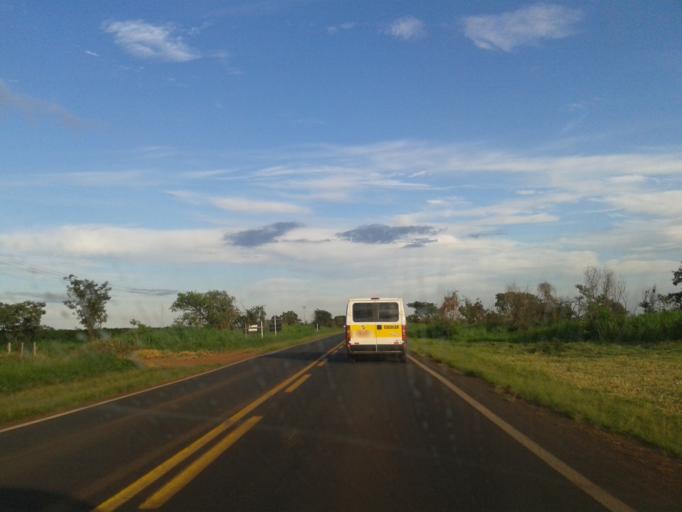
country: BR
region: Minas Gerais
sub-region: Araguari
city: Araguari
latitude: -18.6383
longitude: -48.2252
